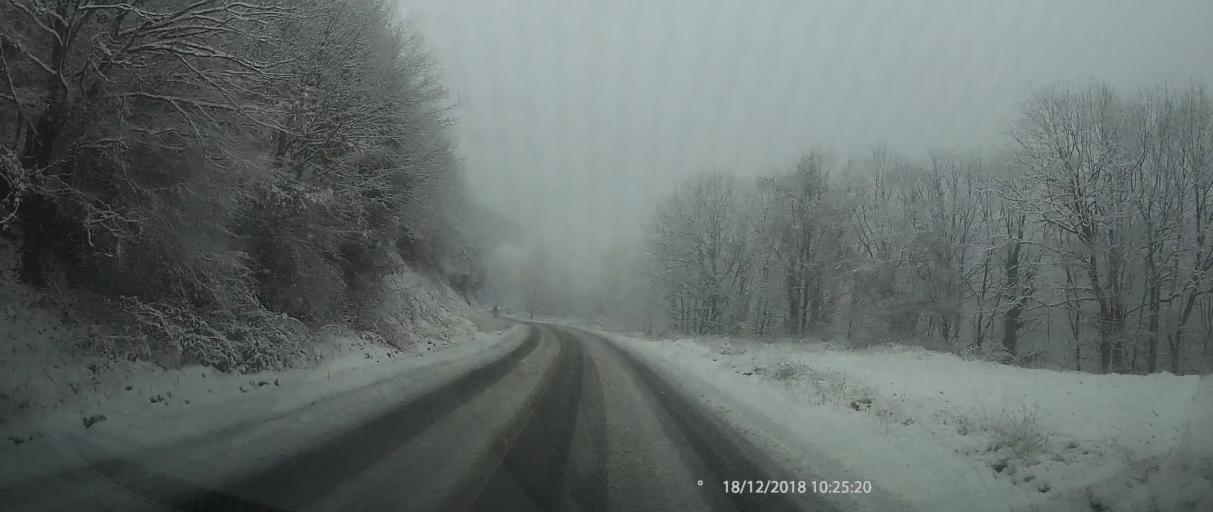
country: GR
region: Thessaly
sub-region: Nomos Larisis
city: Livadi
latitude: 40.1650
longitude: 22.2471
